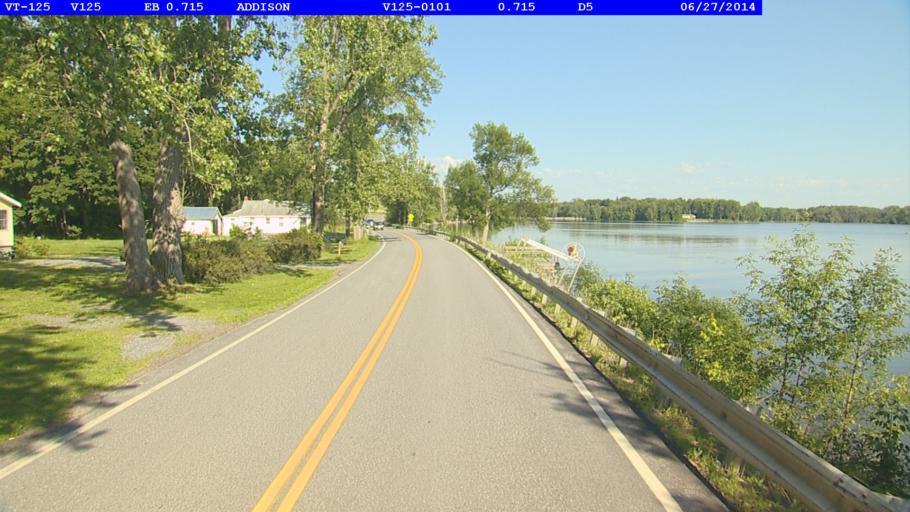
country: US
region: New York
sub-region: Essex County
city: Port Henry
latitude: 44.0307
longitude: -73.4067
